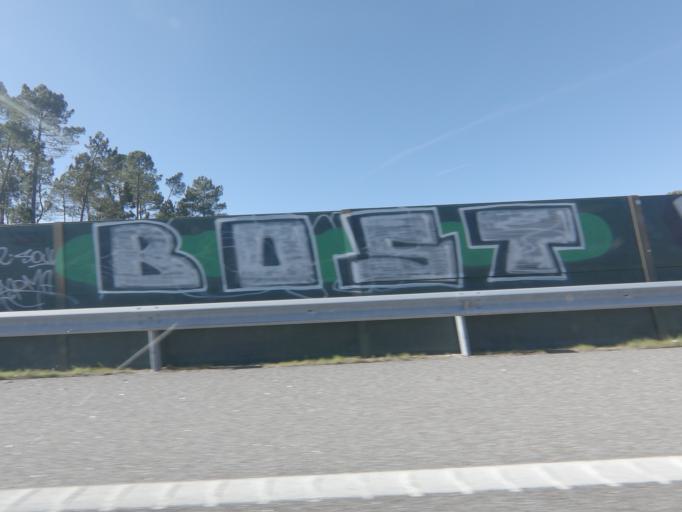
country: ES
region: Galicia
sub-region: Provincia de Ourense
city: Cea
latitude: 42.4643
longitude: -8.0269
